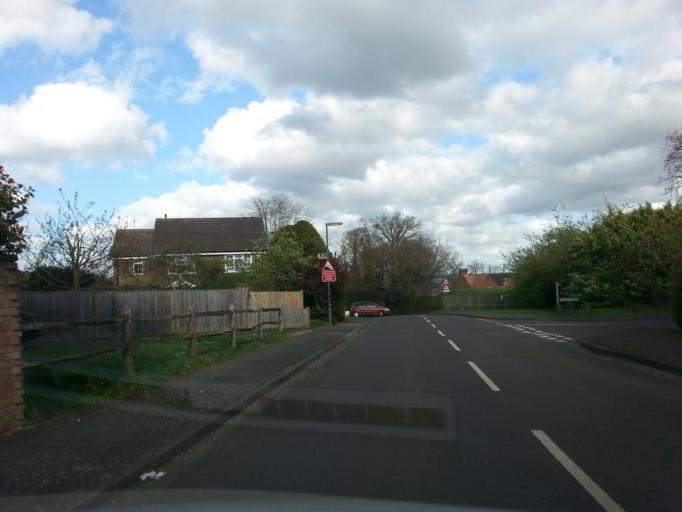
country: GB
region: England
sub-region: Surrey
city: Godalming
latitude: 51.1964
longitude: -0.6161
